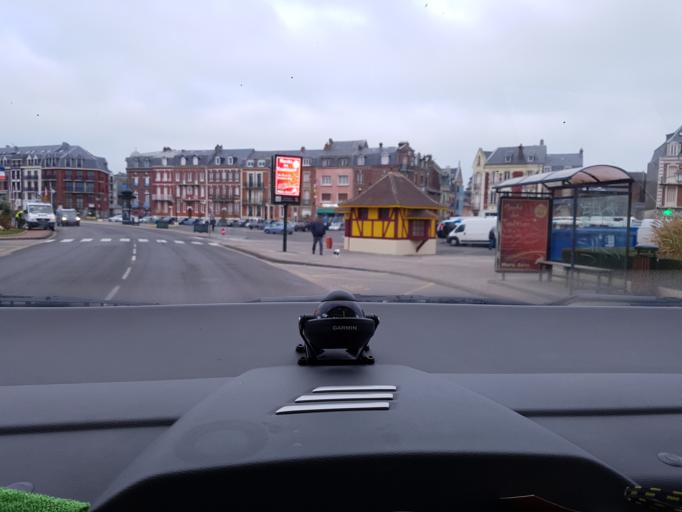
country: FR
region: Picardie
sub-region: Departement de la Somme
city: Mers-les-Bains
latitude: 50.0664
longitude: 1.3865
